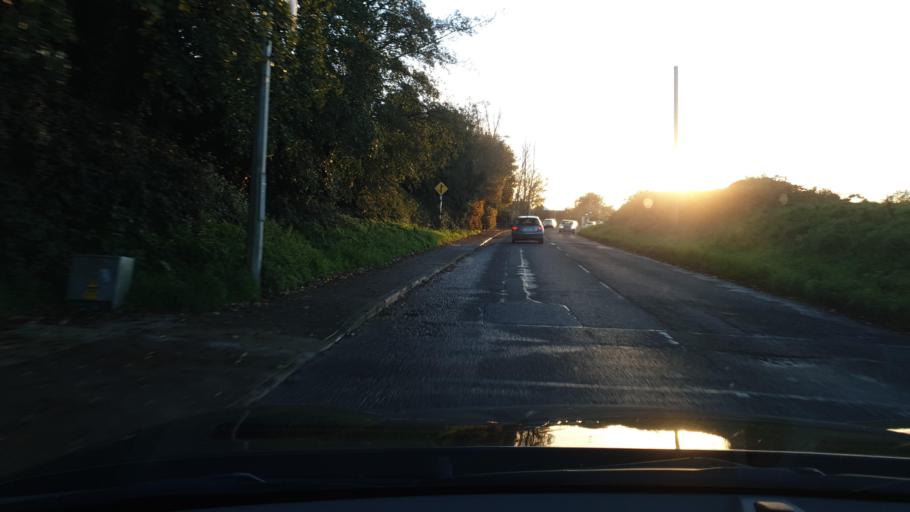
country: IE
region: Leinster
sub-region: Lu
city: Drogheda
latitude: 53.7264
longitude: -6.3273
